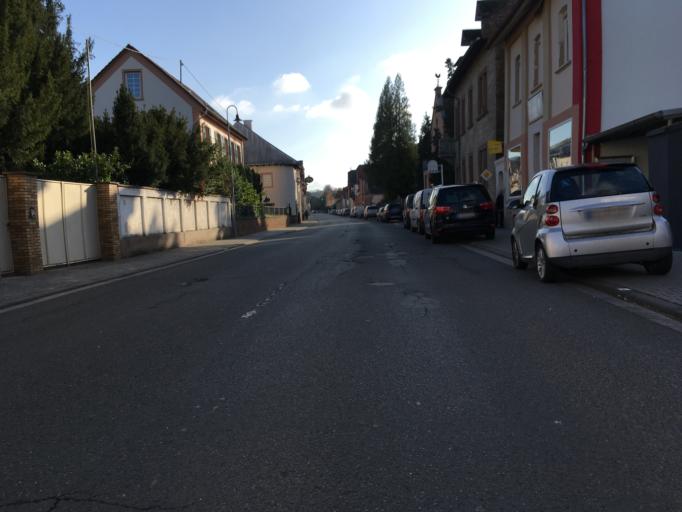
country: DE
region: Rheinland-Pfalz
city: Bodenheim
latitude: 49.9285
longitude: 8.3127
